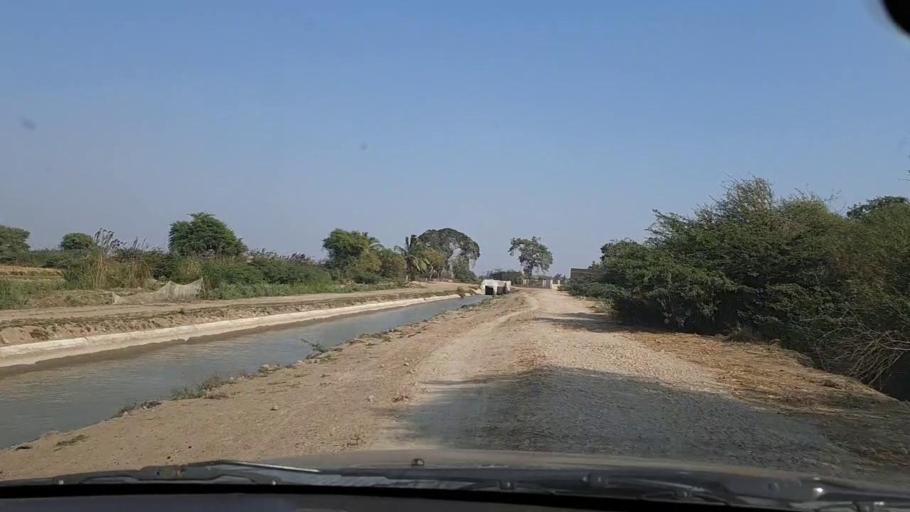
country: PK
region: Sindh
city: Mirpur Sakro
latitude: 24.3421
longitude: 67.7323
